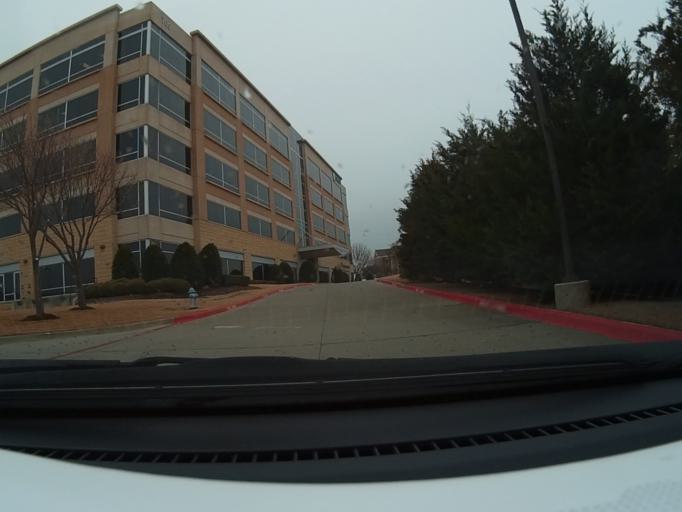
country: US
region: Texas
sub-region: Collin County
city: Allen
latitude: 33.0935
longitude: -96.6826
